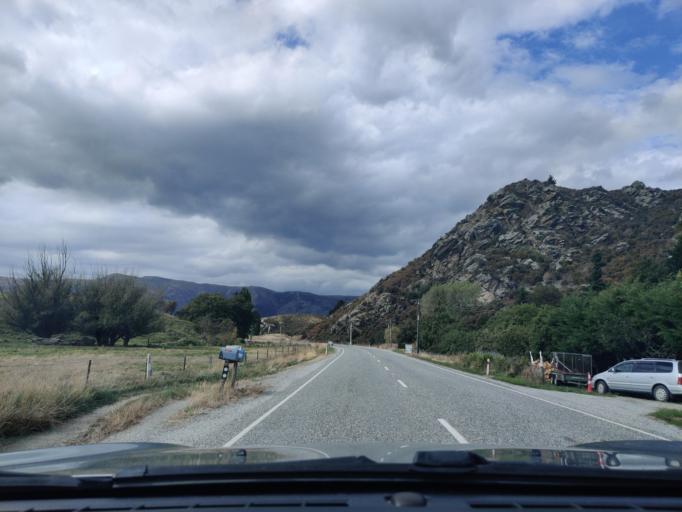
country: NZ
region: Otago
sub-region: Queenstown-Lakes District
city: Wanaka
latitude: -44.7517
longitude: 169.2850
